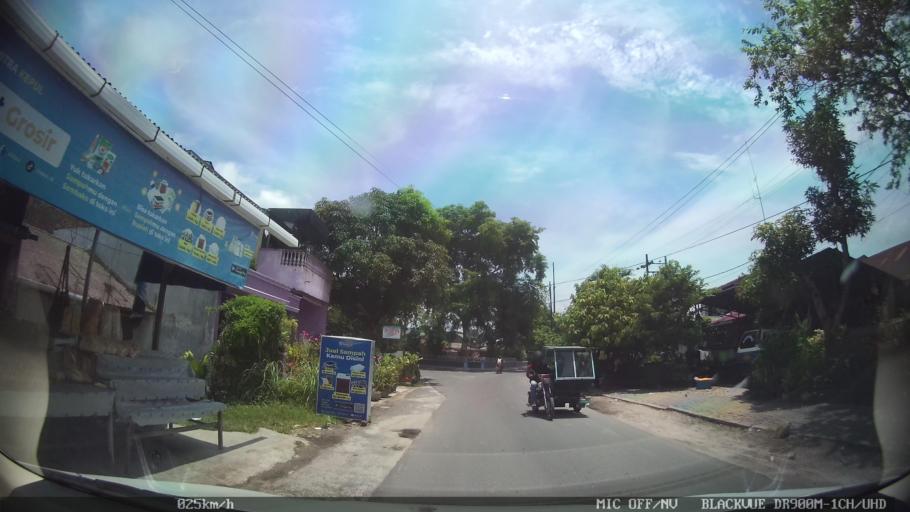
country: ID
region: North Sumatra
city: Percut
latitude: 3.5422
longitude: 98.8758
